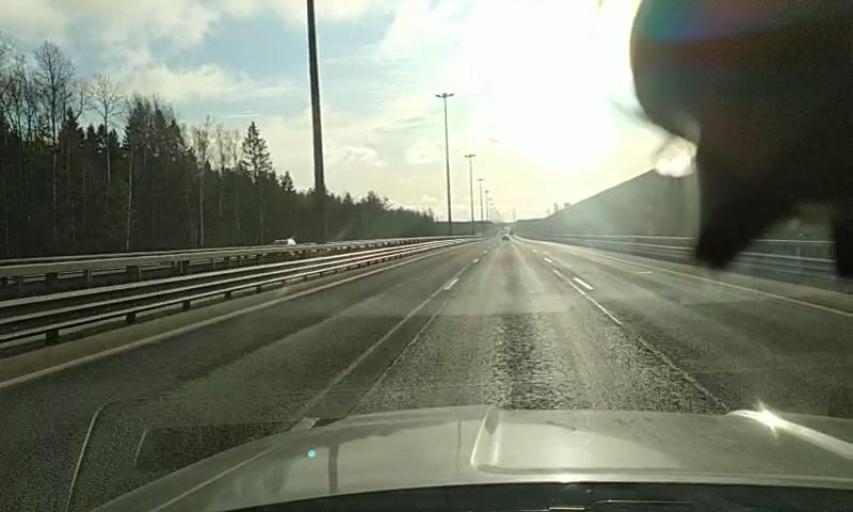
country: RU
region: St.-Petersburg
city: Pesochnyy
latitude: 60.1129
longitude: 30.0806
